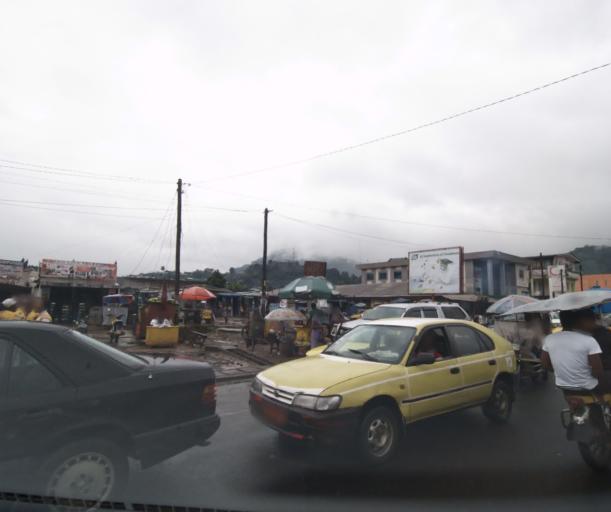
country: CM
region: South-West Province
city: Limbe
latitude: 4.0152
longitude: 9.2091
